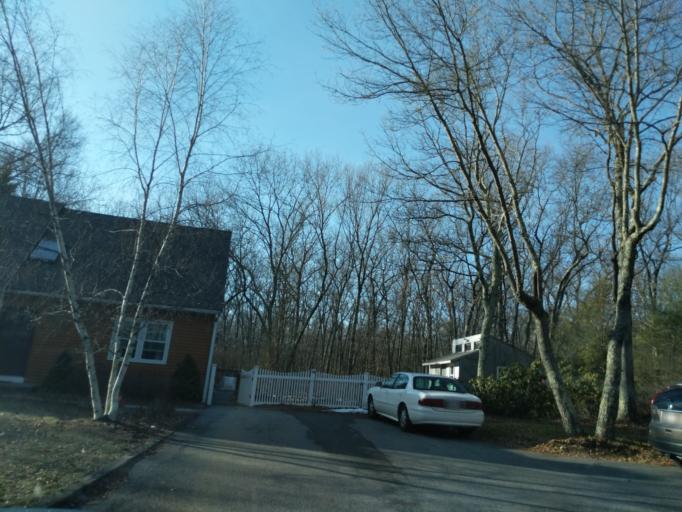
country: US
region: Massachusetts
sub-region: Worcester County
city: Blackstone
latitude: 42.0507
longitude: -71.5091
